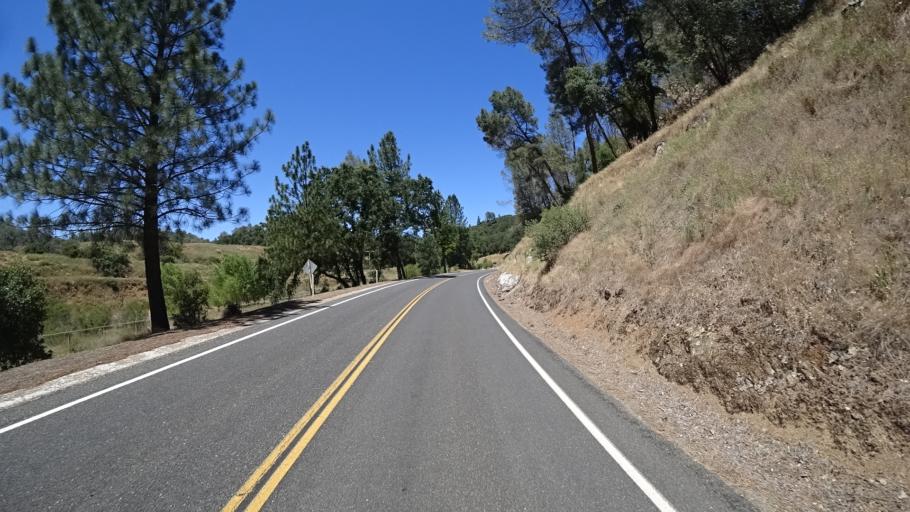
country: US
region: California
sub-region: Calaveras County
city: San Andreas
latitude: 38.1656
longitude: -120.6718
